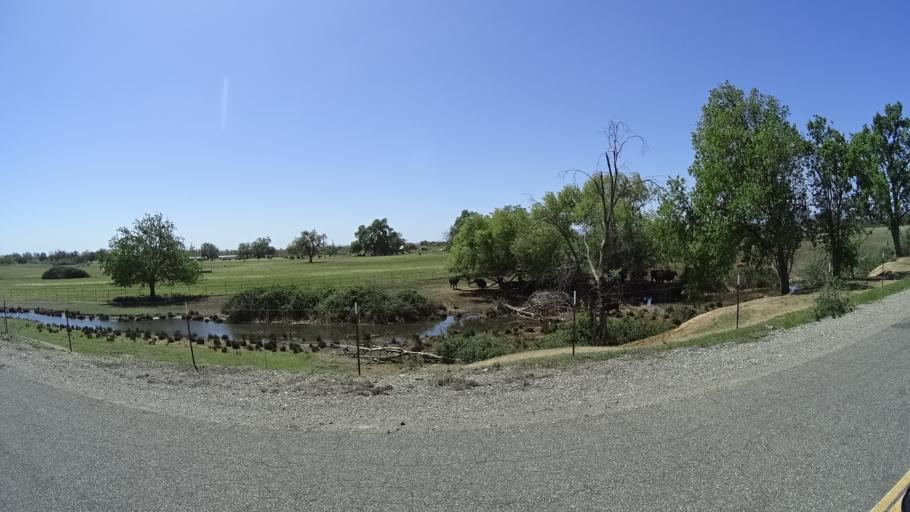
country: US
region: California
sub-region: Glenn County
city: Orland
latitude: 39.7880
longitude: -122.2220
